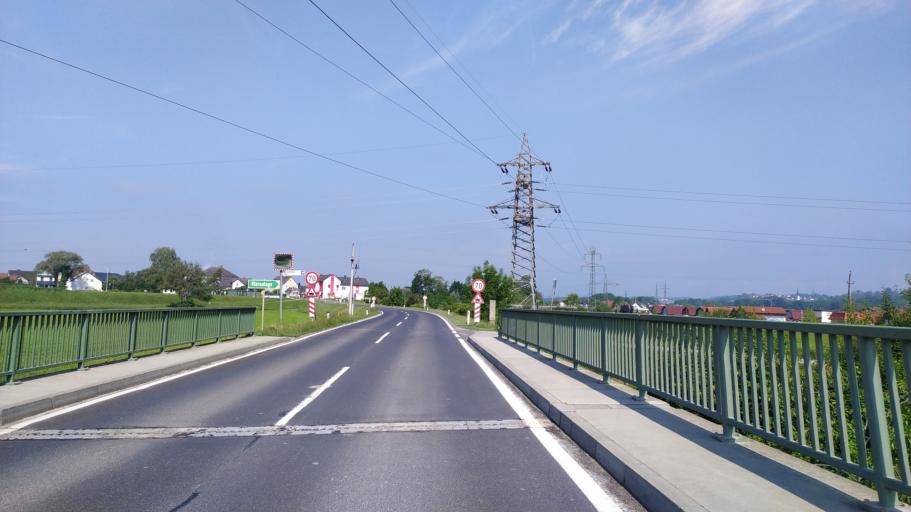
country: AT
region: Lower Austria
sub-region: Politischer Bezirk Amstetten
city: Ennsdorf
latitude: 48.2268
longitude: 14.5320
